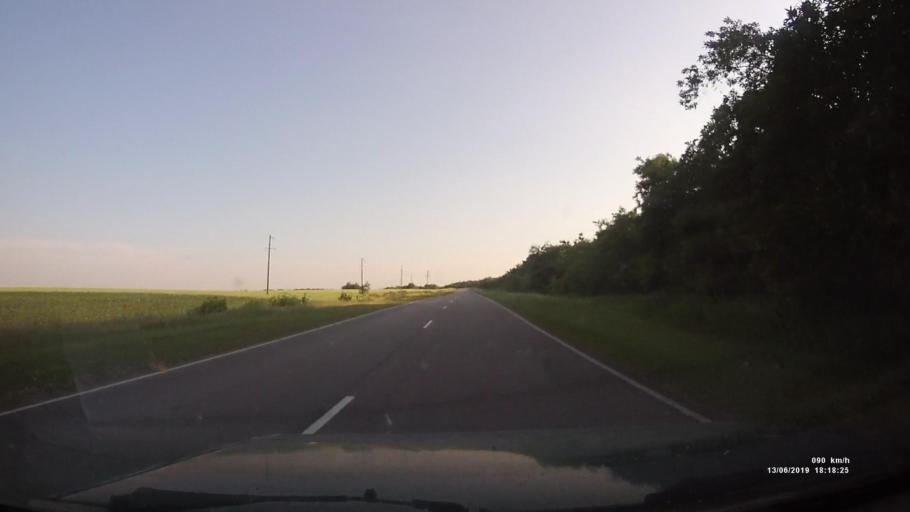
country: RU
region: Rostov
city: Kazanskaya
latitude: 49.9081
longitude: 41.3141
